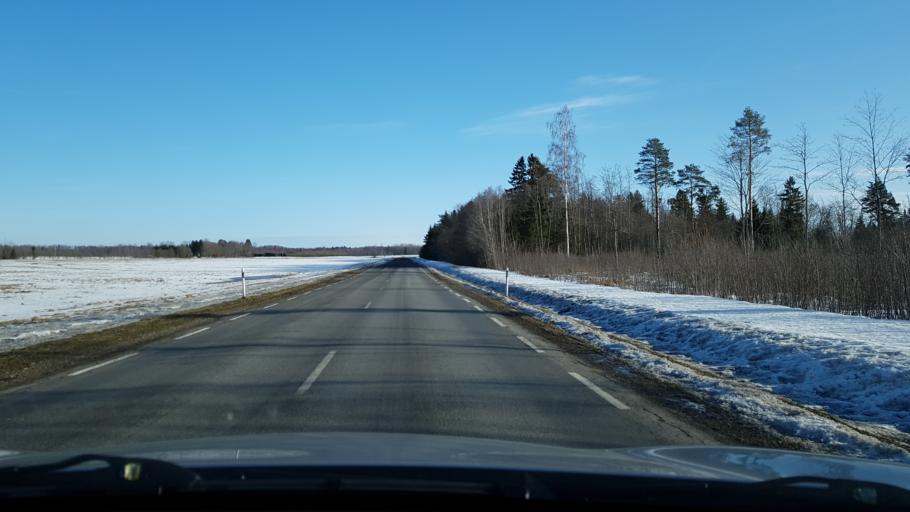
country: EE
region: Viljandimaa
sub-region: Vohma linn
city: Vohma
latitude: 58.6378
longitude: 25.6621
